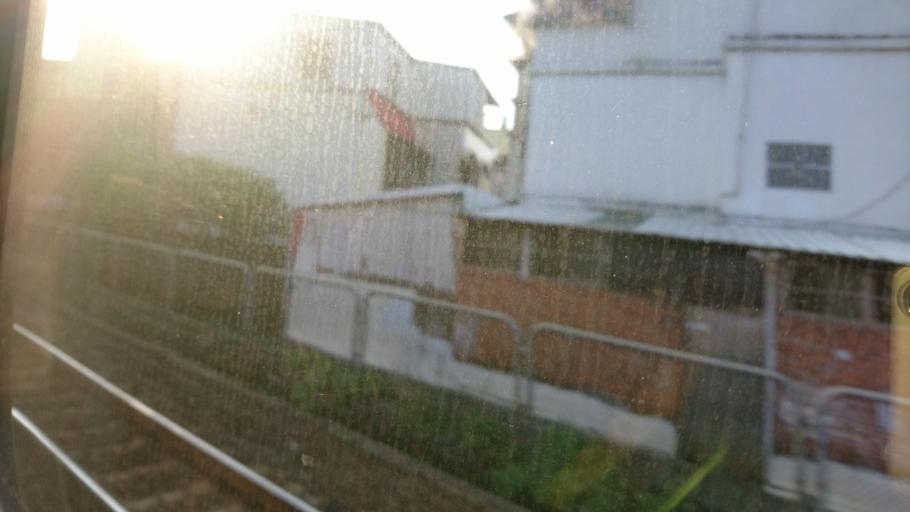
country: TW
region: Taiwan
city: Taoyuan City
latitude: 24.9485
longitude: 121.2189
